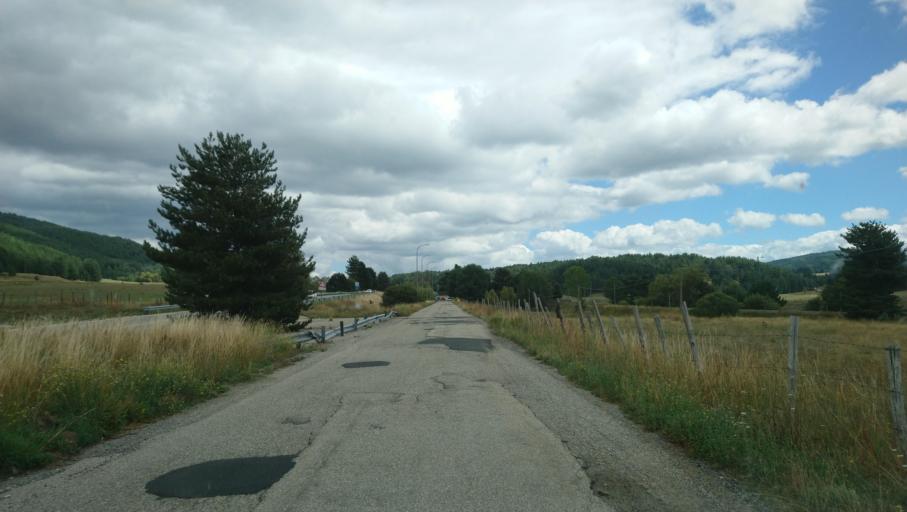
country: IT
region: Calabria
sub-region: Provincia di Cosenza
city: Longobucco
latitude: 39.3158
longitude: 16.5475
